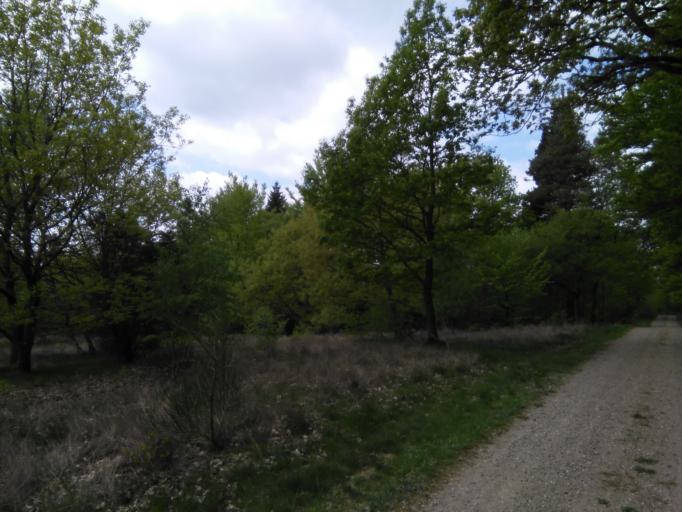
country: DK
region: Central Jutland
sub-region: Silkeborg Kommune
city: Svejbaek
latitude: 56.0635
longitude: 9.6136
